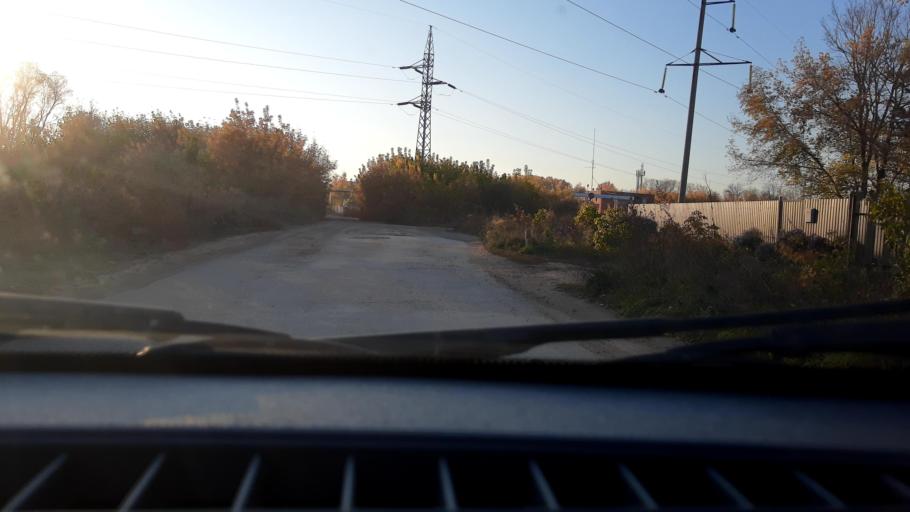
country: RU
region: Bashkortostan
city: Ufa
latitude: 54.7994
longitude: 56.1621
